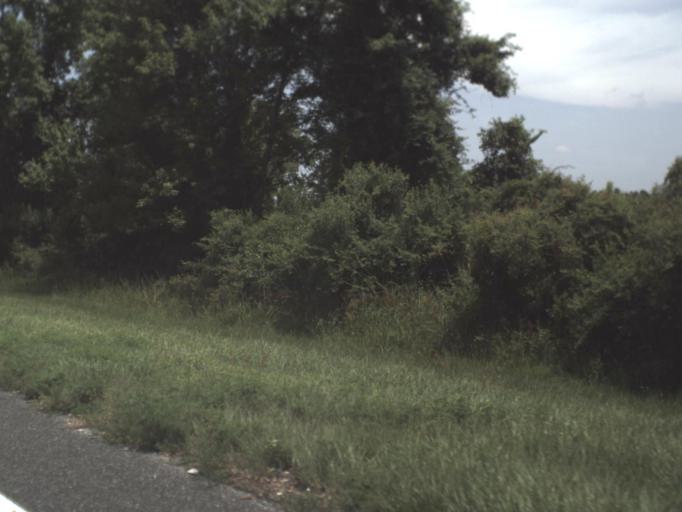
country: US
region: Florida
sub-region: Taylor County
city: Steinhatchee
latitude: 29.8288
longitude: -83.3596
